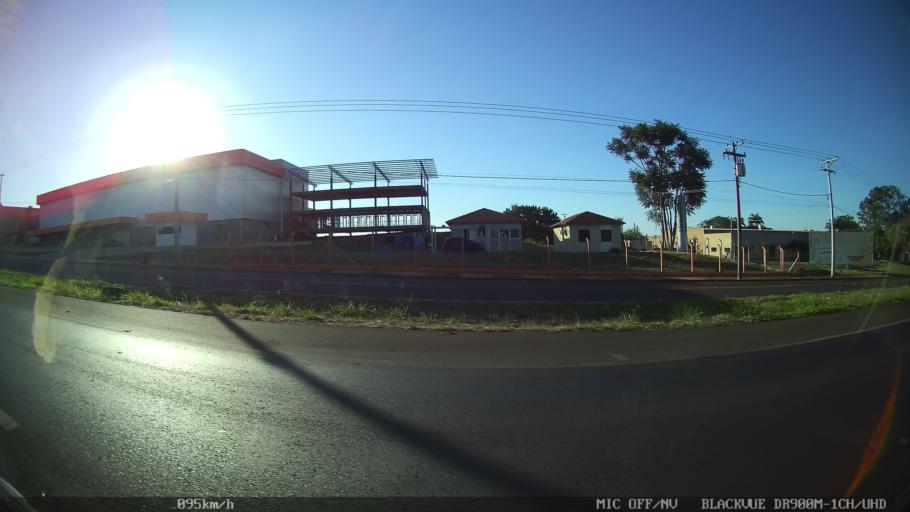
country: BR
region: Sao Paulo
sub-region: Guapiacu
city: Guapiacu
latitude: -20.7849
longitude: -49.2733
